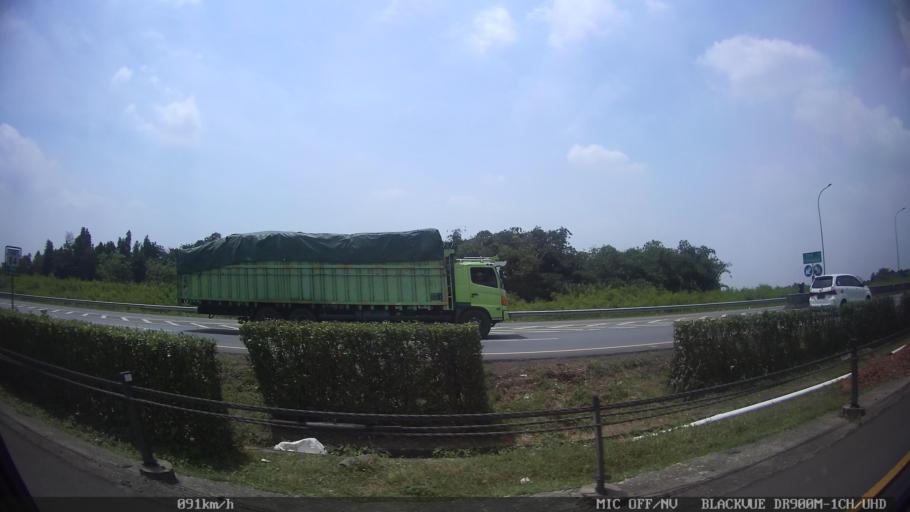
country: ID
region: Banten
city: Serang
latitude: -6.1386
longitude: 106.2415
